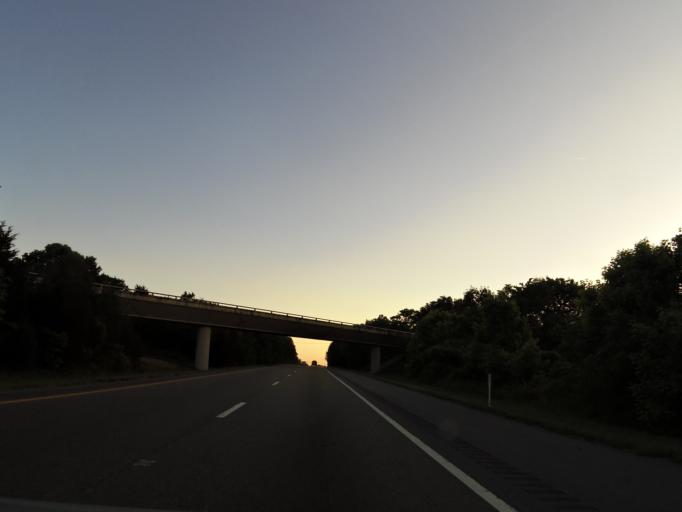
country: US
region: Tennessee
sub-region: Greene County
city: Mosheim
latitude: 36.2505
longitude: -82.9697
